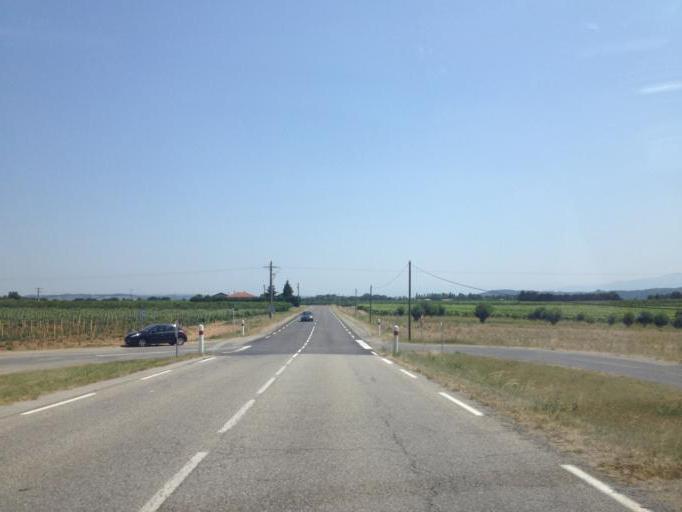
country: FR
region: Rhone-Alpes
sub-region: Departement de la Drome
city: La Roche-de-Glun
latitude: 45.0113
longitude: 4.8764
